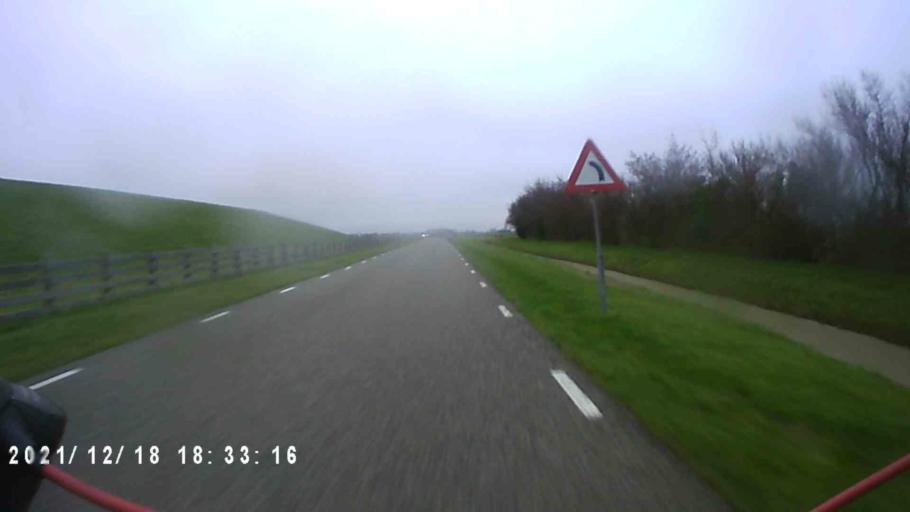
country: NL
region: Friesland
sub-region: Gemeente Dongeradeel
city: Ternaard
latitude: 53.4015
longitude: 6.0218
